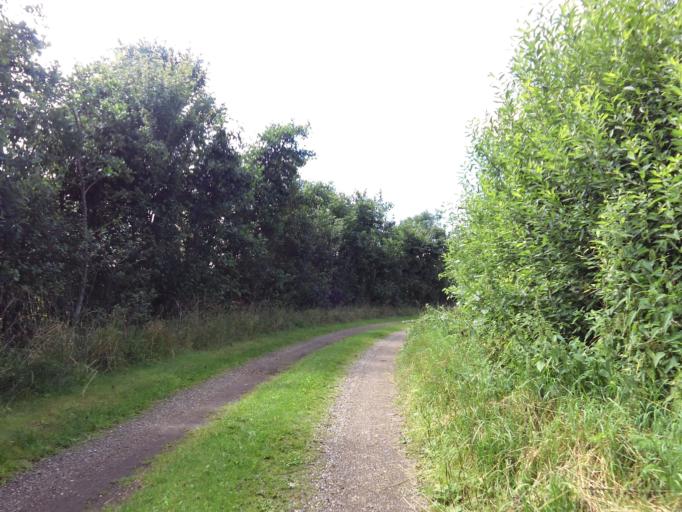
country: DK
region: South Denmark
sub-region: Esbjerg Kommune
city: Ribe
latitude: 55.3013
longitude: 8.7938
